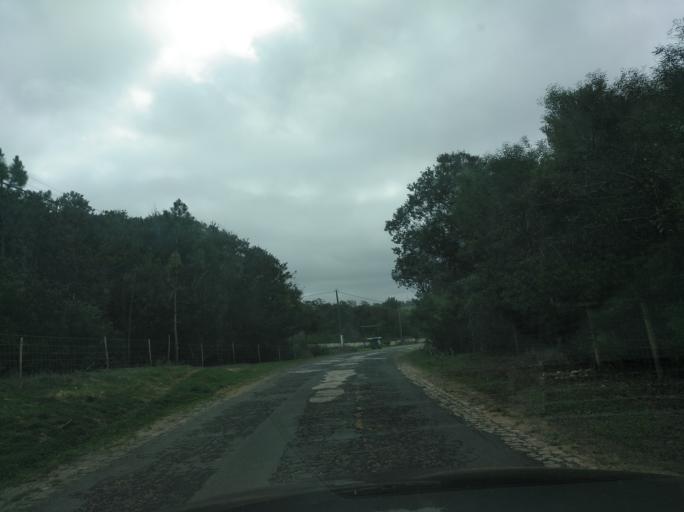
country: PT
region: Setubal
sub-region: Sines
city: Porto Covo
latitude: 37.8326
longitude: -8.7869
